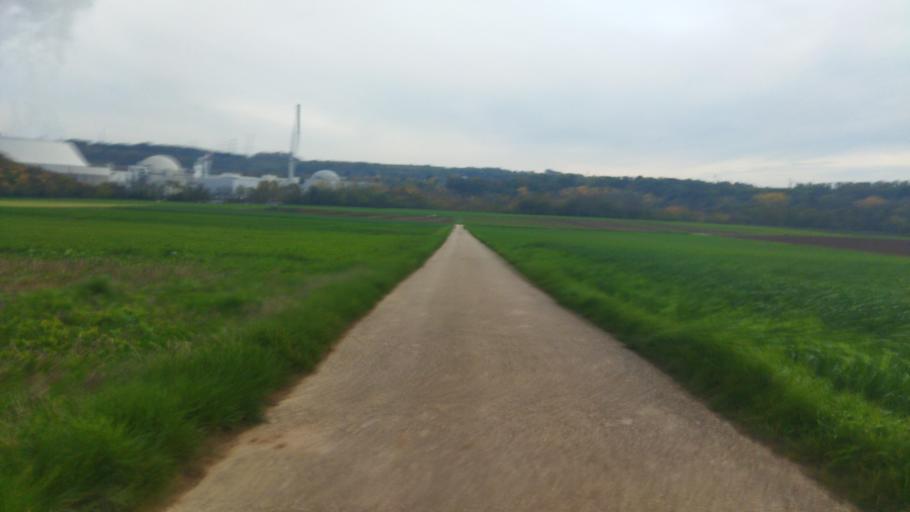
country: DE
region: Baden-Wuerttemberg
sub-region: Regierungsbezirk Stuttgart
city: Neckarwestheim
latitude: 49.0496
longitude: 9.1664
